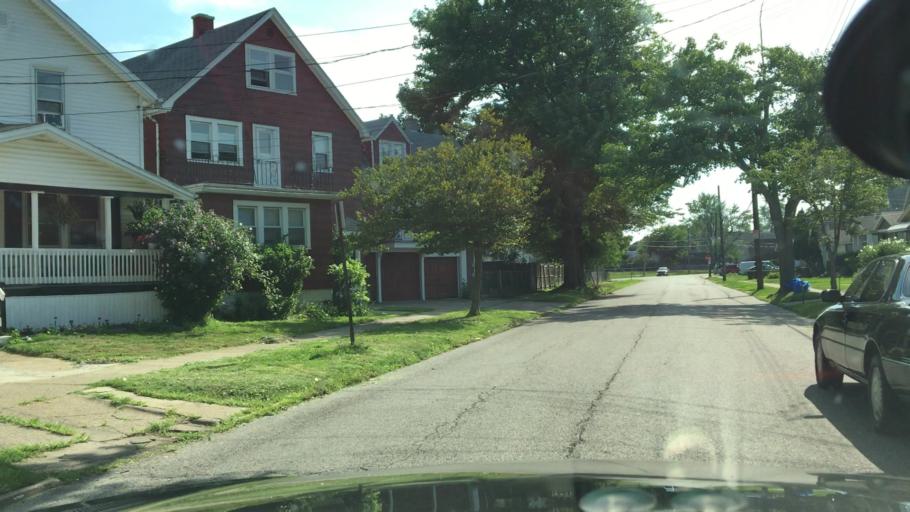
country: US
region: New York
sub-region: Erie County
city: Eggertsville
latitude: 42.9380
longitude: -78.8113
